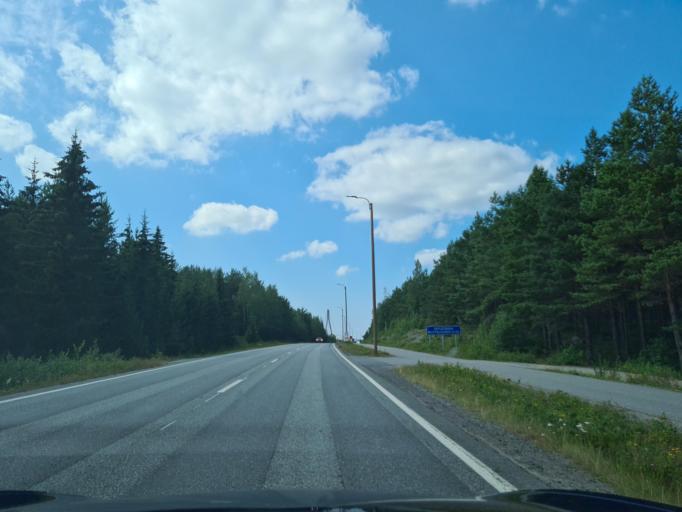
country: FI
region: Ostrobothnia
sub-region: Vaasa
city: Replot
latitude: 63.2055
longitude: 21.4986
